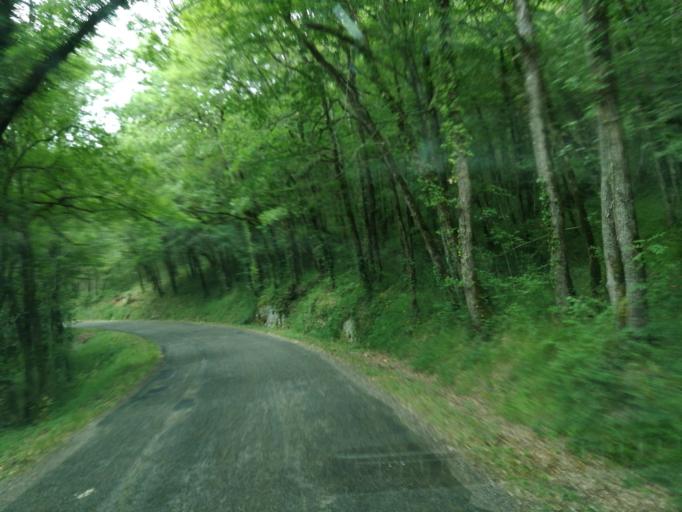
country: FR
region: Aquitaine
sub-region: Departement du Lot-et-Garonne
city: Montayral
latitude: 44.5476
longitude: 1.0727
